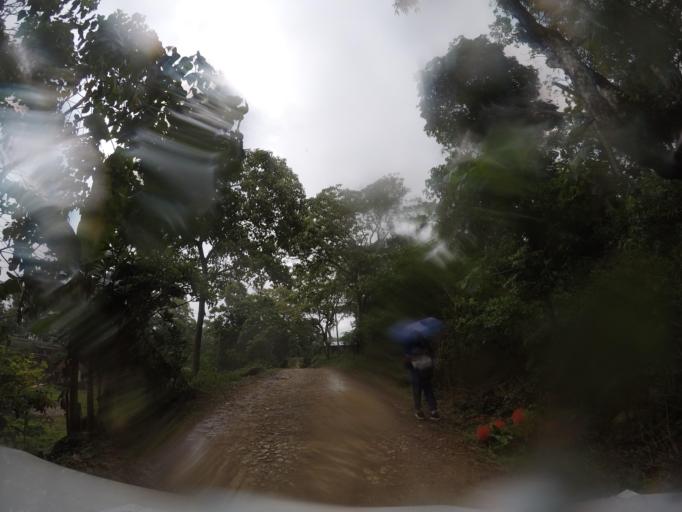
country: TL
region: Baucau
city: Venilale
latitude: -8.6420
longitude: 126.3952
